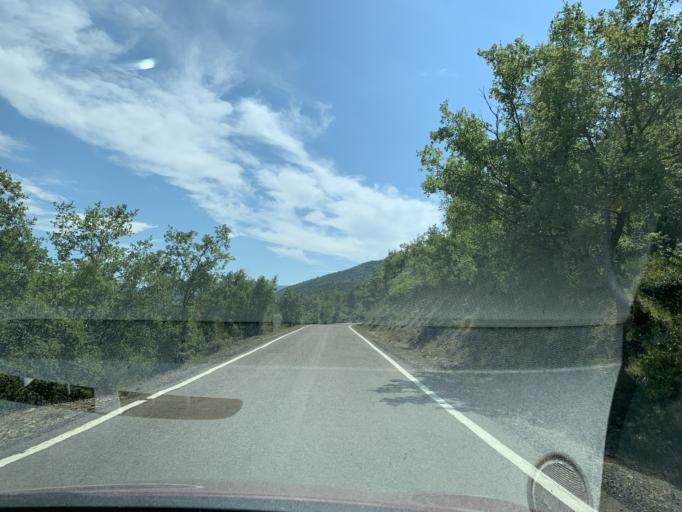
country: ES
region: Aragon
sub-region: Provincia de Huesca
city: Jasa
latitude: 42.6164
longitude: -0.6611
